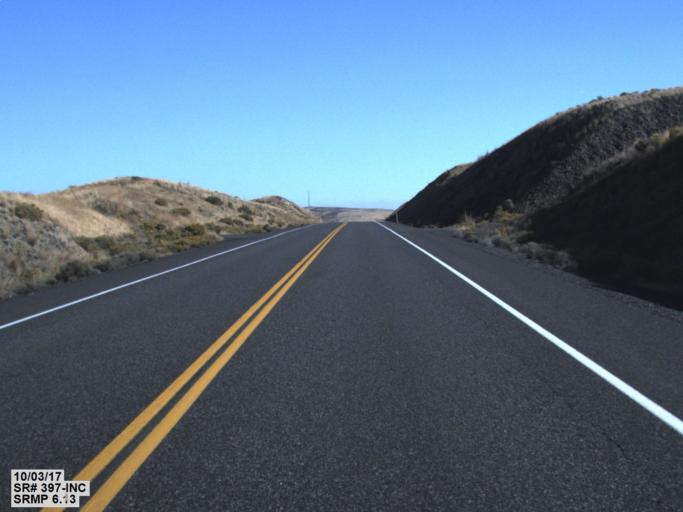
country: US
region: Washington
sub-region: Benton County
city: Highland
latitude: 46.1332
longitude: -119.0878
